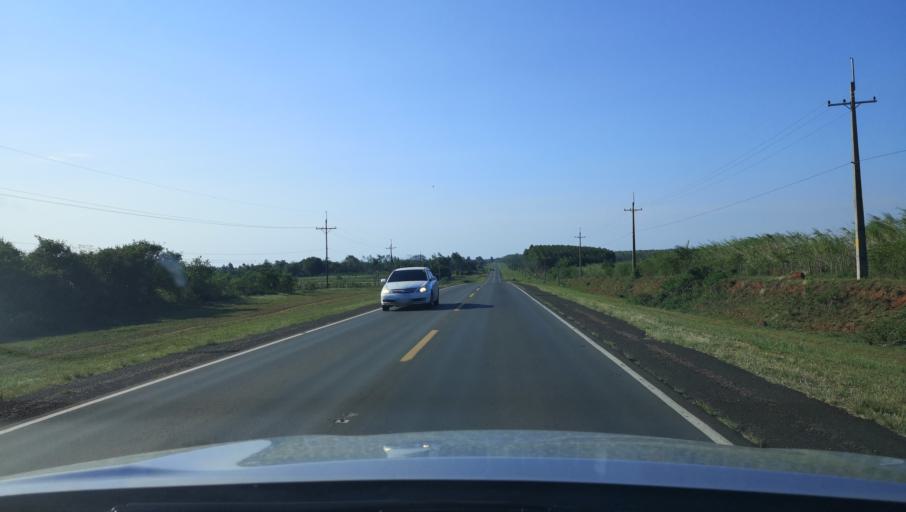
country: PY
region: Misiones
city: Santa Maria
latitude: -26.7780
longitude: -57.0285
